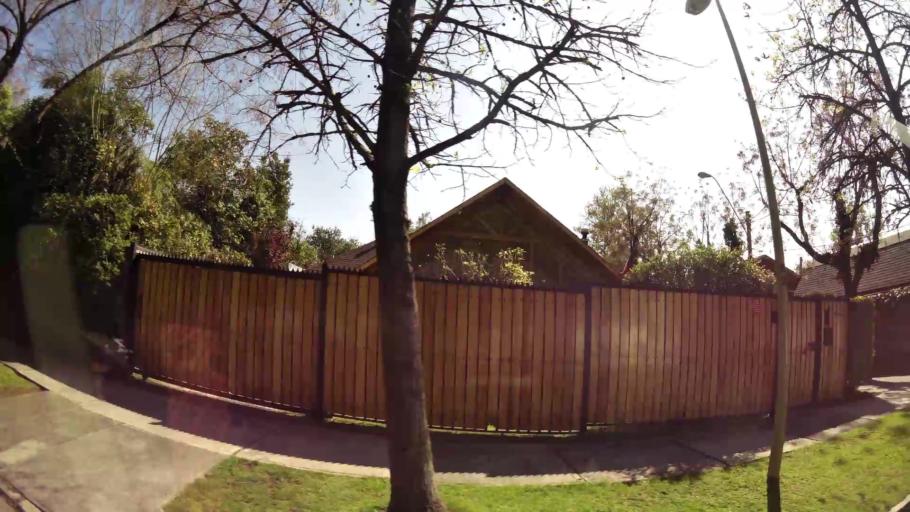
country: CL
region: Santiago Metropolitan
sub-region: Provincia de Santiago
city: Villa Presidente Frei, Nunoa, Santiago, Chile
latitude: -33.3984
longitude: -70.5411
